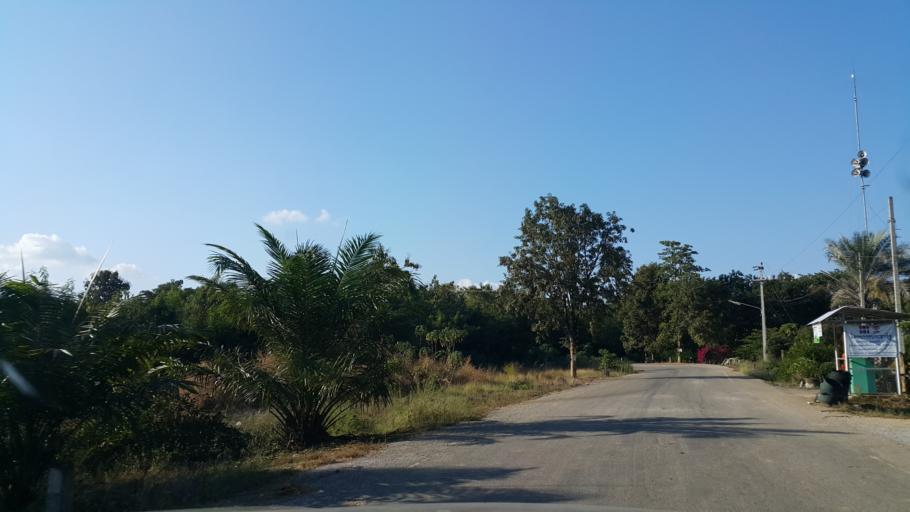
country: TH
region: Sukhothai
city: Thung Saliam
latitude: 17.3856
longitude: 99.5208
